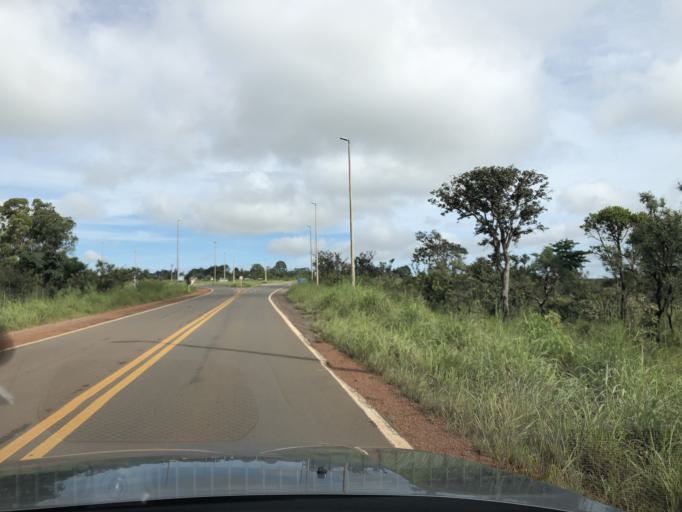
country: BR
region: Federal District
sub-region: Brasilia
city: Brasilia
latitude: -15.7305
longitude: -48.0830
